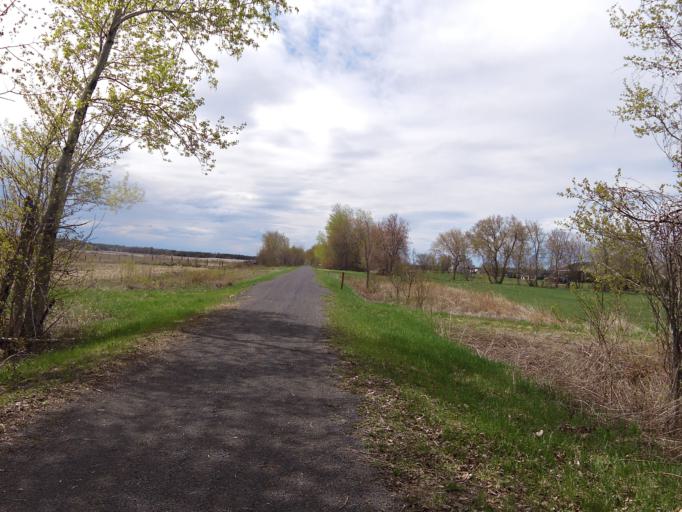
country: CA
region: Ontario
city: Hawkesbury
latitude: 45.5398
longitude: -74.7387
